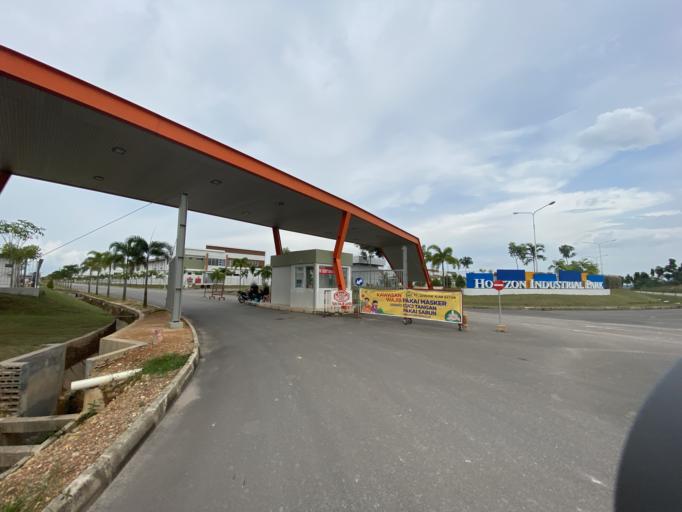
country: SG
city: Singapore
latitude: 1.0215
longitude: 103.9466
